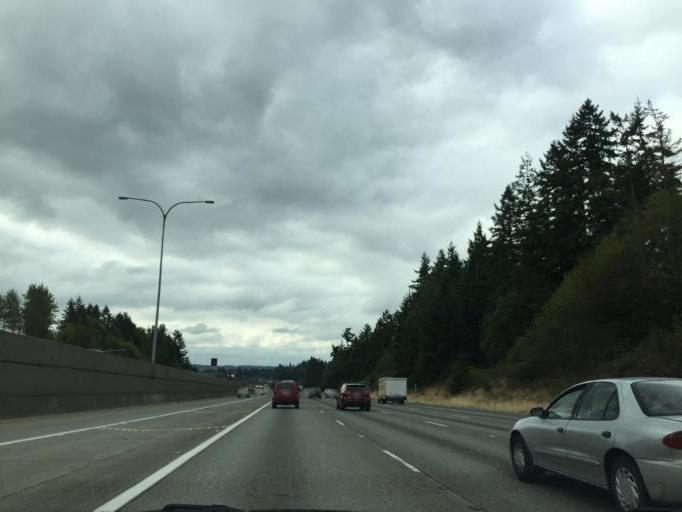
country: US
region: Washington
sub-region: Pierce County
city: Milton
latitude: 47.2645
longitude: -122.3233
